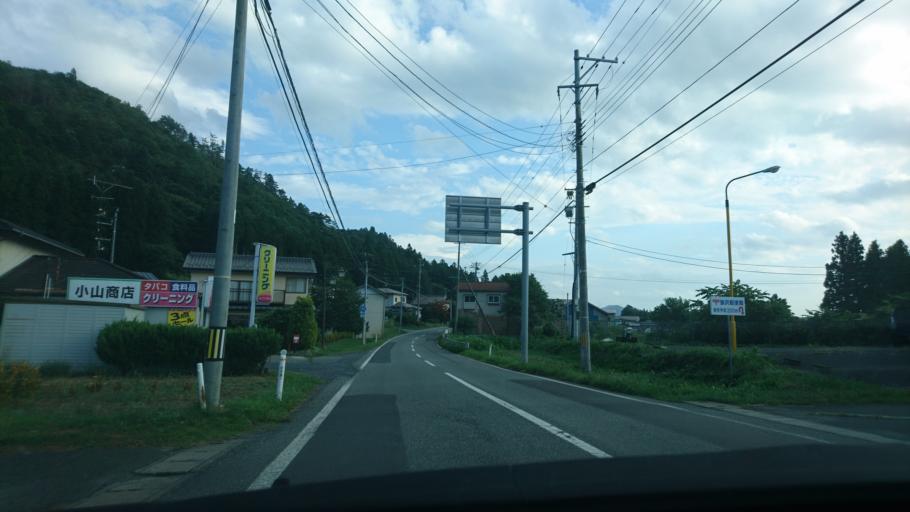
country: JP
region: Iwate
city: Mizusawa
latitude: 39.0329
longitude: 141.2954
